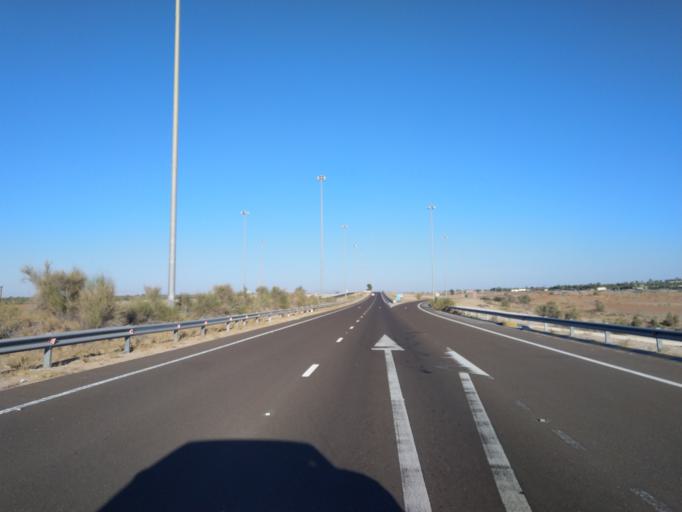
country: OM
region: Al Buraimi
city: Al Buraymi
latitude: 24.5378
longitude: 55.5977
